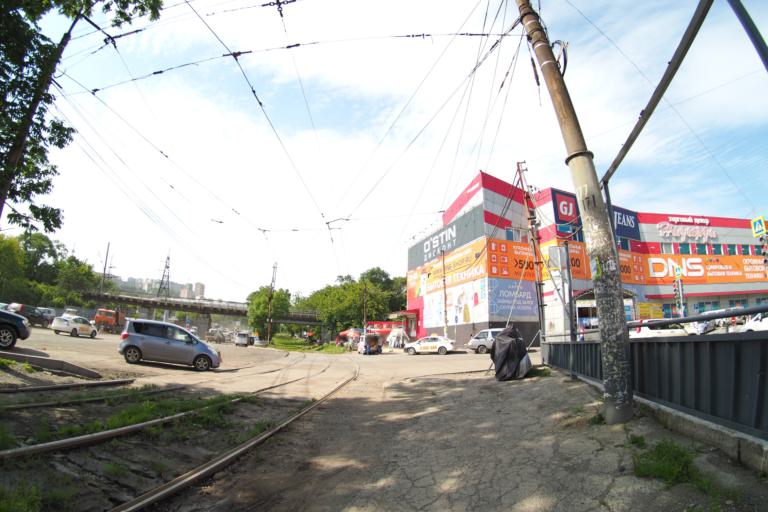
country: RU
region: Primorskiy
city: Vladivostok
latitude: 43.1072
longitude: 131.9395
